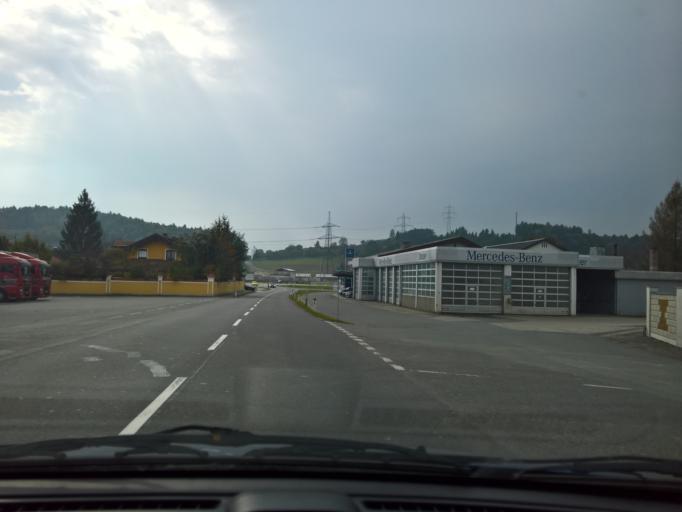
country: AT
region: Styria
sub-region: Politischer Bezirk Deutschlandsberg
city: Gross Sankt Florian
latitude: 46.8171
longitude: 15.3158
